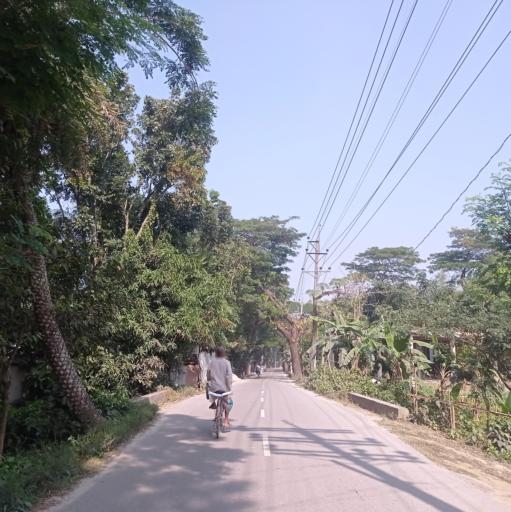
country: BD
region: Dhaka
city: Narsingdi
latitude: 24.0505
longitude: 90.6819
